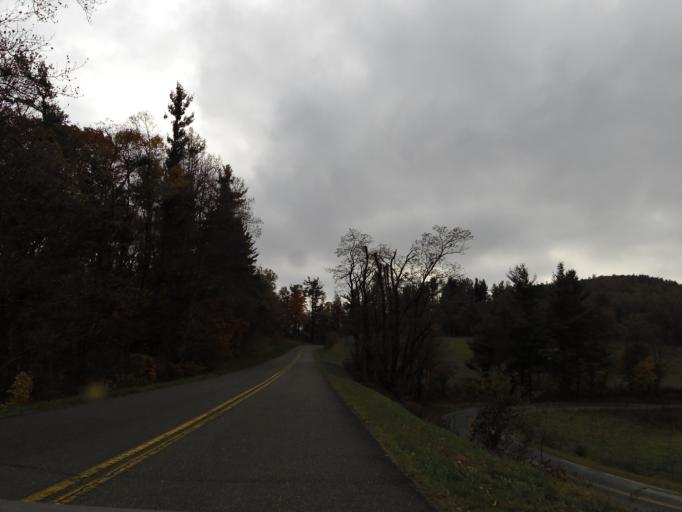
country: US
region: North Carolina
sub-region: Ashe County
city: West Jefferson
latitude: 36.2644
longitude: -81.4350
